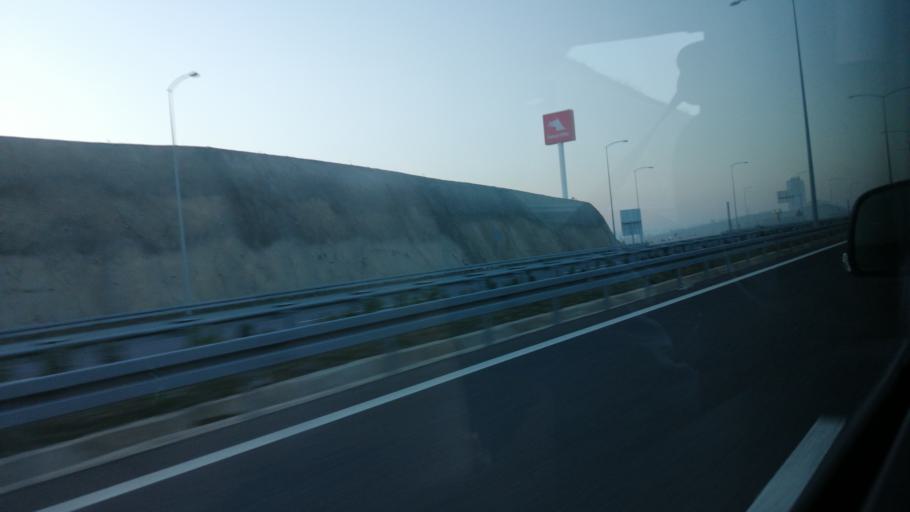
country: TR
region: Kocaeli
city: Tavsanli
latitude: 40.7800
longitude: 29.5176
